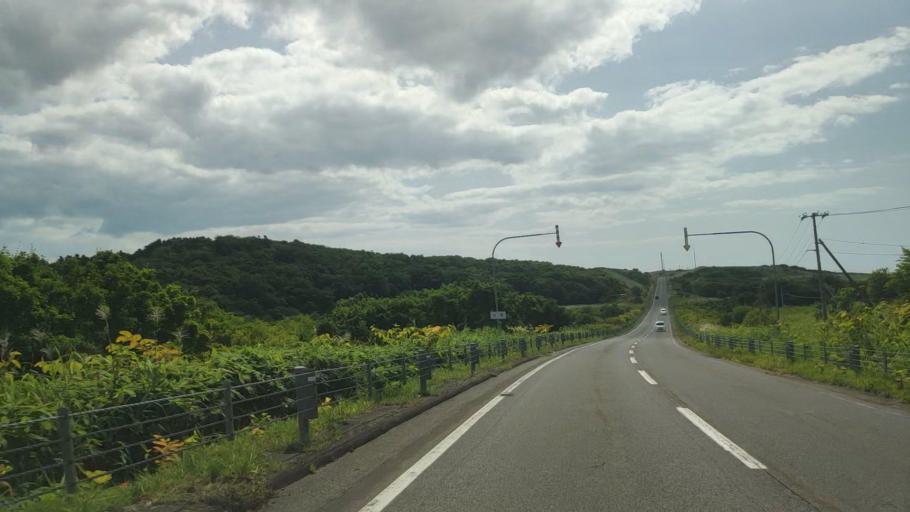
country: JP
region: Hokkaido
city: Rumoi
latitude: 44.6075
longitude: 141.7981
